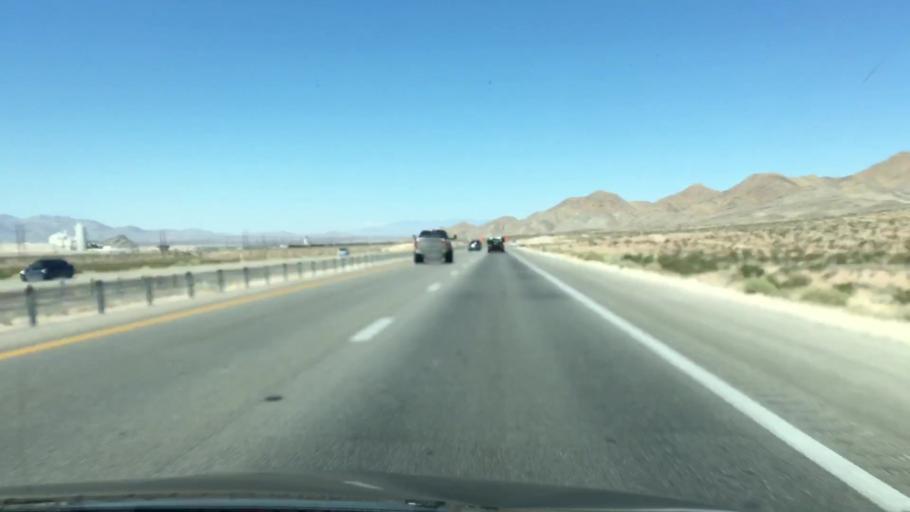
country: US
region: Nevada
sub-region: Clark County
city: Nellis Air Force Base
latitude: 36.3407
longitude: -114.9146
